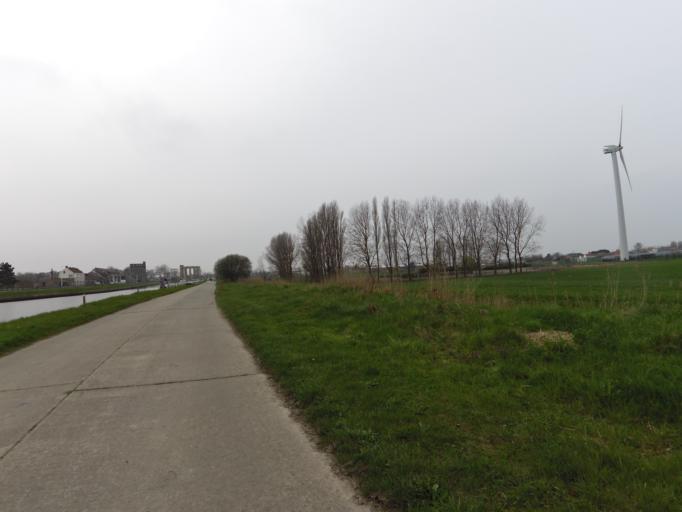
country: BE
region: Flanders
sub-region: Provincie West-Vlaanderen
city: Nieuwpoort
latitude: 51.1385
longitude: 2.7636
